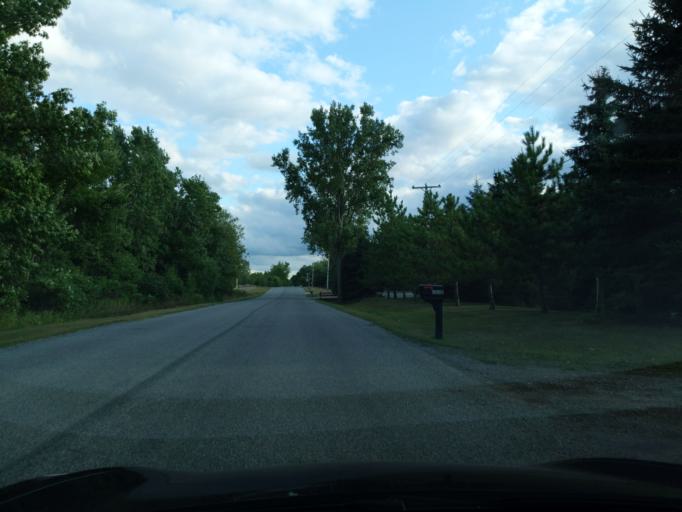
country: US
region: Michigan
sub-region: Eaton County
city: Dimondale
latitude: 42.6372
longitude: -84.5825
